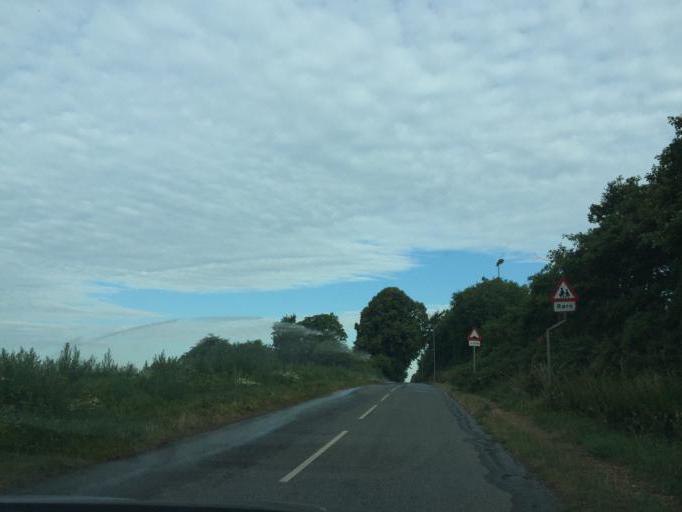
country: DK
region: South Denmark
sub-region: Assens Kommune
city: Assens
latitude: 55.2391
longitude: 9.9786
